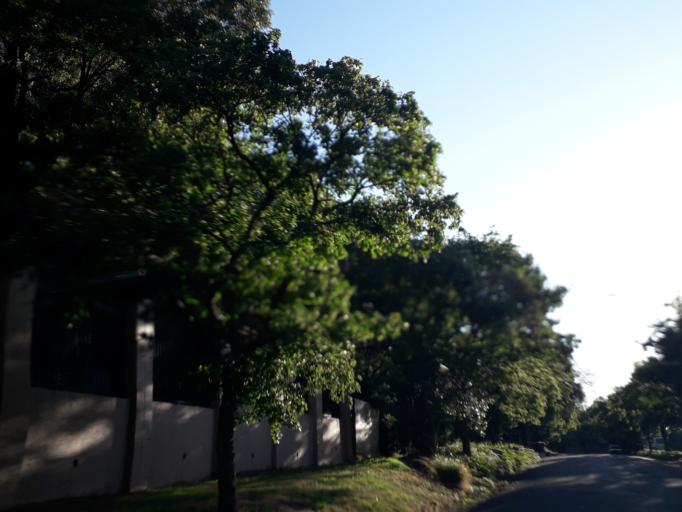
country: ZA
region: Gauteng
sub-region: City of Johannesburg Metropolitan Municipality
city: Johannesburg
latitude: -26.1802
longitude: 28.0262
